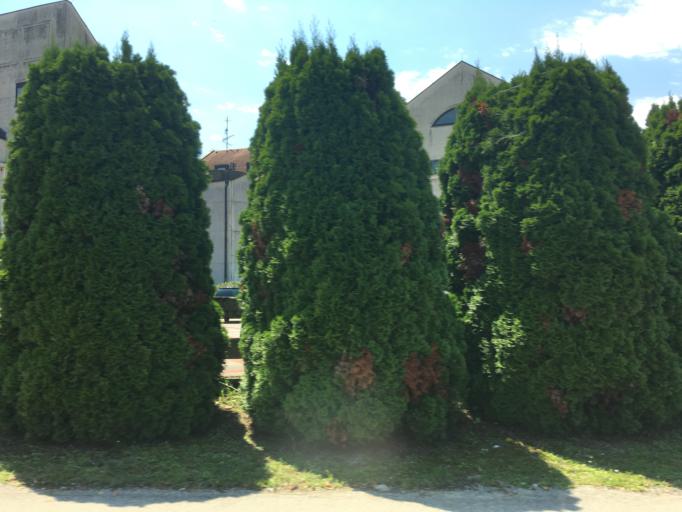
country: SI
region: Metlika
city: Metlika
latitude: 45.6461
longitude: 15.3170
